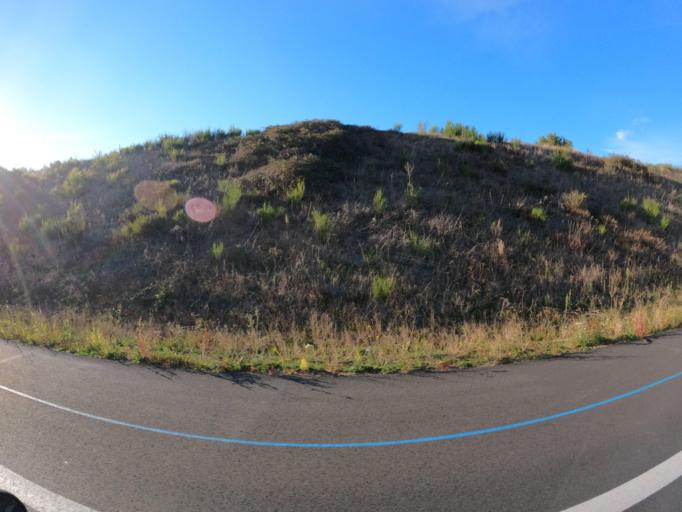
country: FR
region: Pays de la Loire
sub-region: Departement de la Vendee
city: Mortagne-sur-Sevre
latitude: 47.0044
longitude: -0.9041
